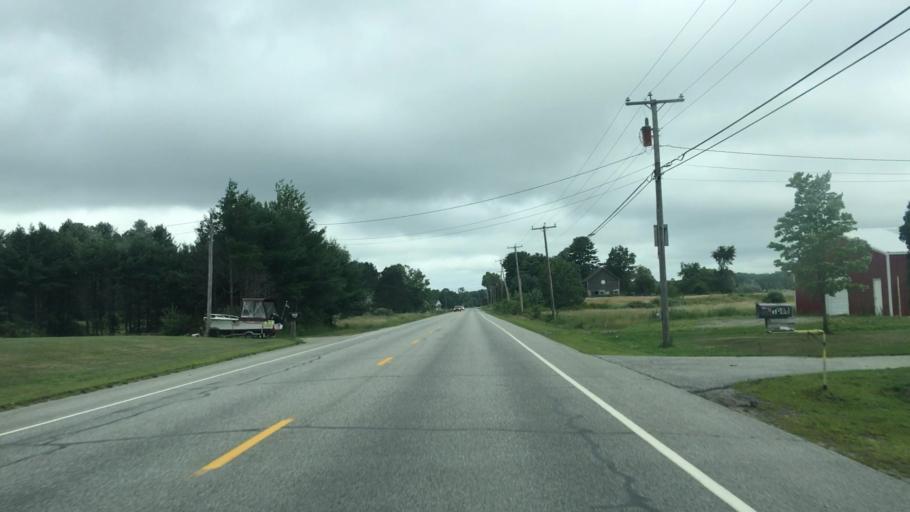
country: US
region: Maine
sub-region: Kennebec County
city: Pittston
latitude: 44.1513
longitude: -69.7439
